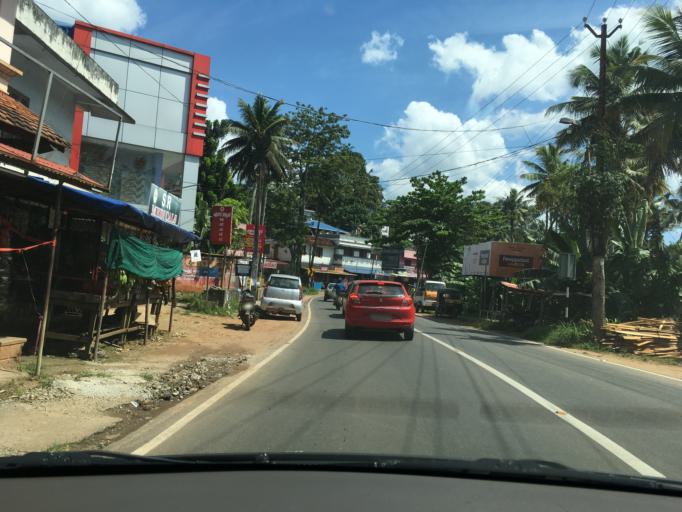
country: IN
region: Kerala
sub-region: Thiruvananthapuram
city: Nedumangad
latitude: 8.5903
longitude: 76.9954
